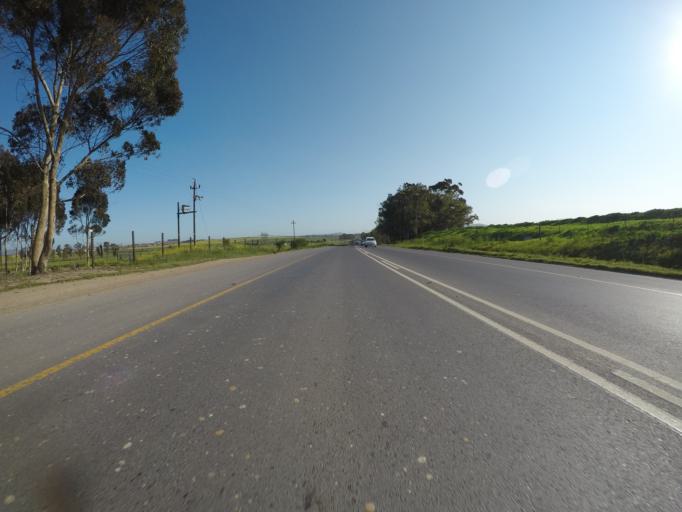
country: ZA
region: Western Cape
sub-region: City of Cape Town
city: Kraaifontein
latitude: -33.7956
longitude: 18.6930
